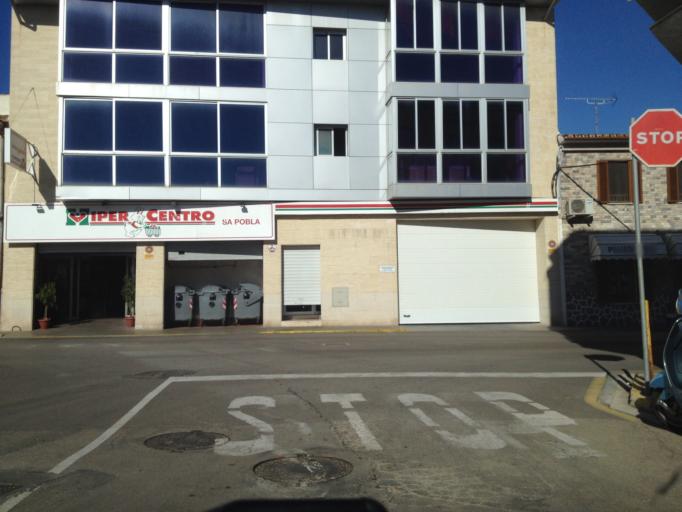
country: ES
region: Balearic Islands
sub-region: Illes Balears
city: sa Pobla
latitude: 39.7708
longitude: 3.0286
